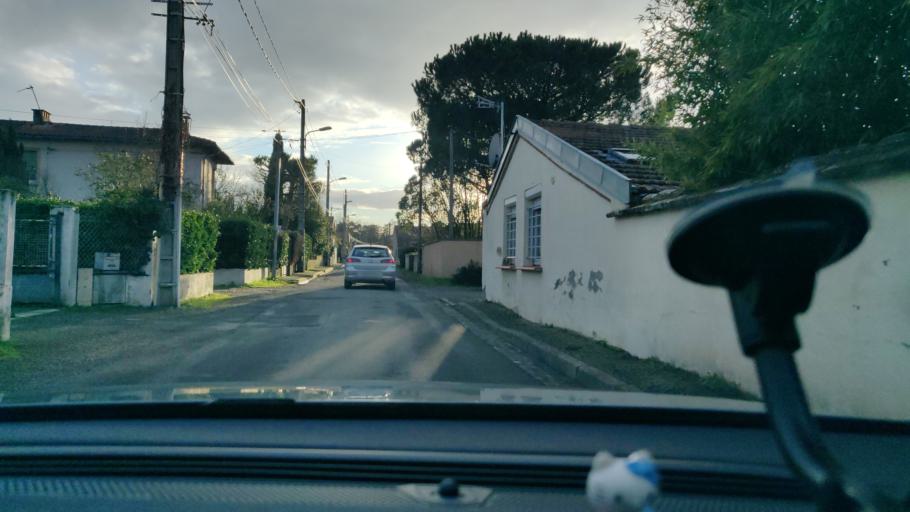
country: FR
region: Midi-Pyrenees
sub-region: Departement de la Haute-Garonne
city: Portet-sur-Garonne
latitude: 43.5552
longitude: 1.3827
